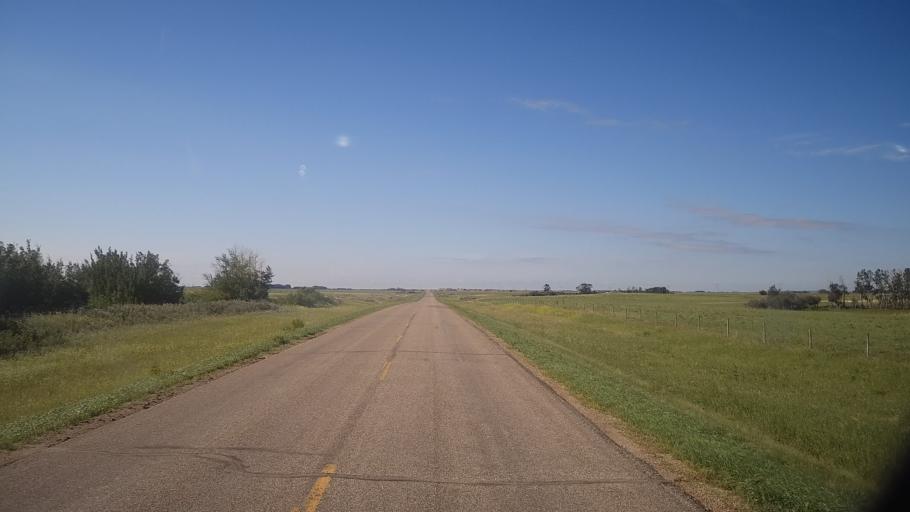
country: CA
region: Saskatchewan
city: Watrous
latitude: 51.7479
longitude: -105.2867
